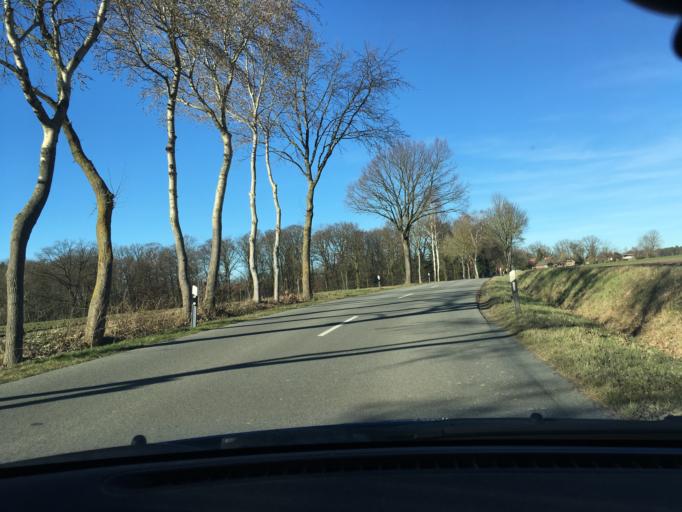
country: DE
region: Lower Saxony
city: Schwienau
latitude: 52.9748
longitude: 10.4480
